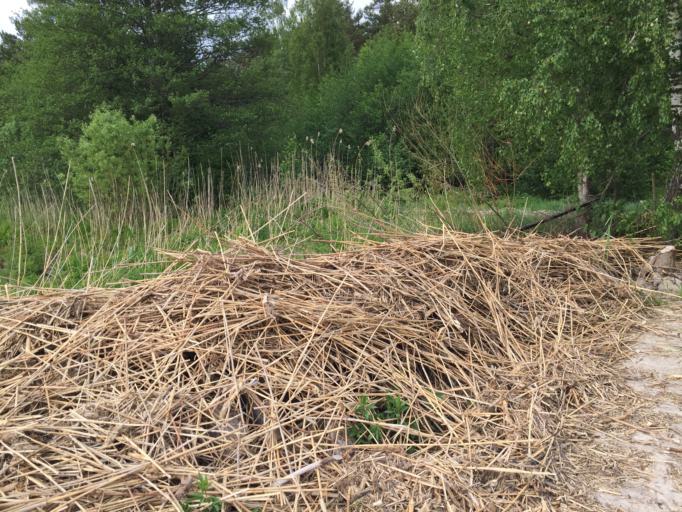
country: LV
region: Riga
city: Bergi
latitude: 57.0264
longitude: 24.3144
